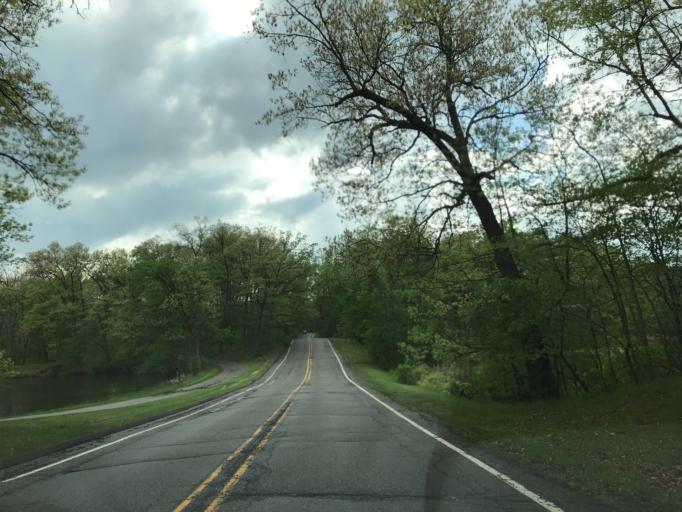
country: US
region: Michigan
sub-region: Oakland County
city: South Lyon
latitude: 42.5350
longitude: -83.6463
